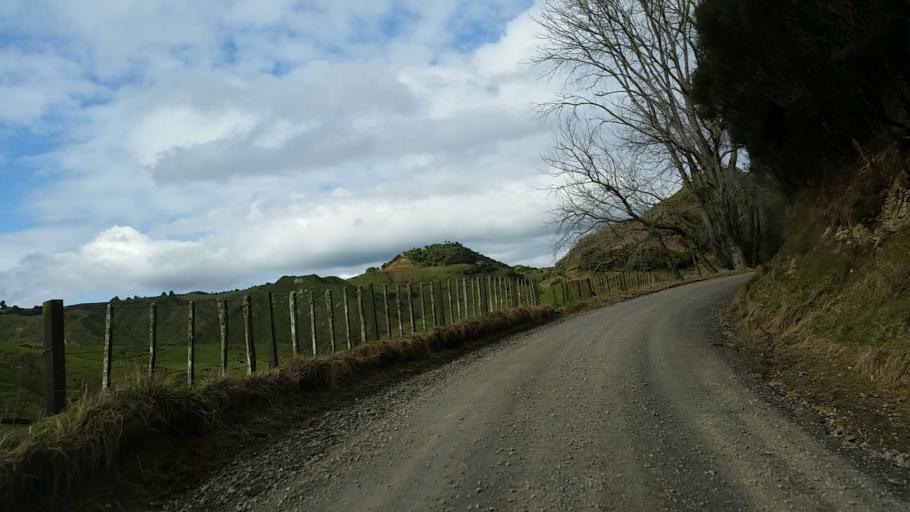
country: NZ
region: Taranaki
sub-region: South Taranaki District
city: Eltham
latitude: -39.1689
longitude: 174.6084
